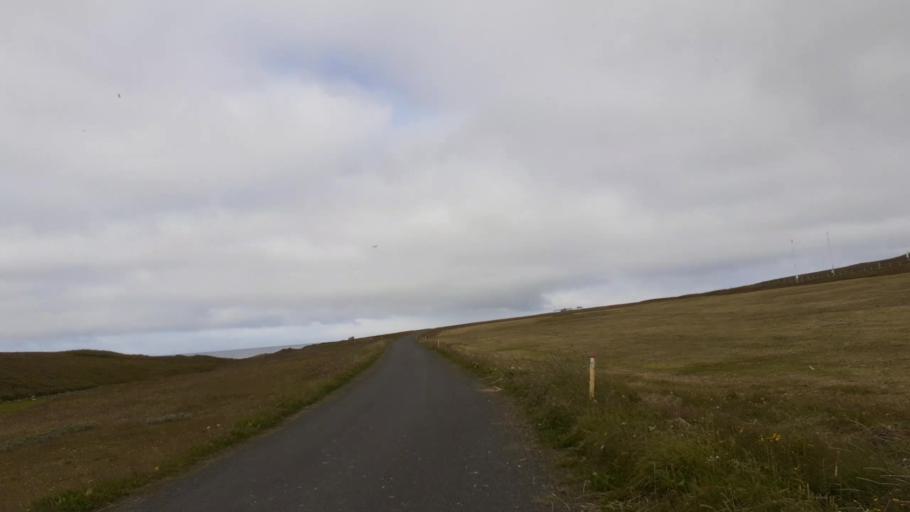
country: IS
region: Northeast
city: Dalvik
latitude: 66.5422
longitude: -18.0167
